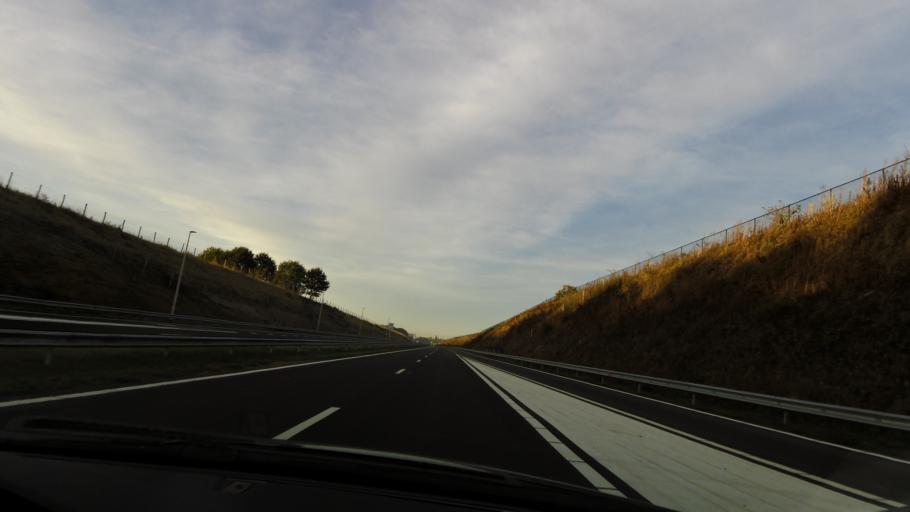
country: NL
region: Limburg
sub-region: Gemeente Onderbanken
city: Merkelbeek
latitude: 50.9440
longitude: 5.9463
